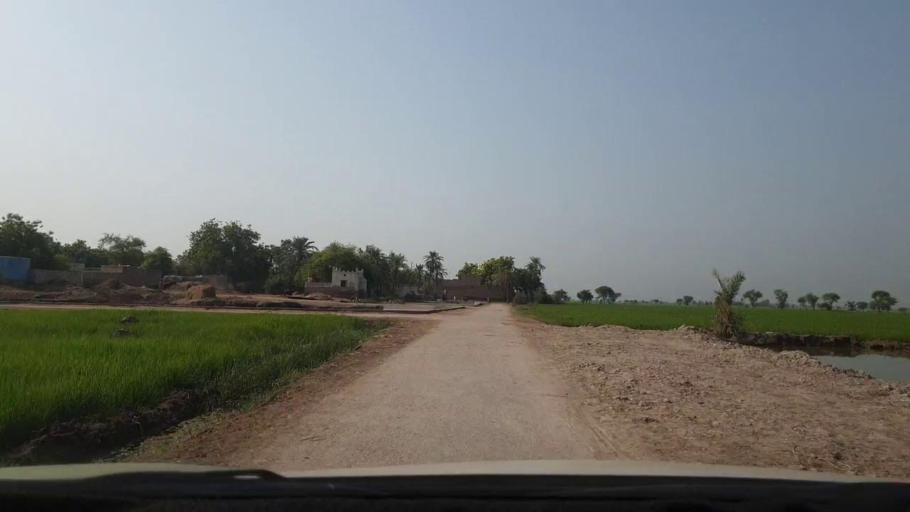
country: PK
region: Sindh
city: Goth Garelo
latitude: 27.4638
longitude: 68.0910
